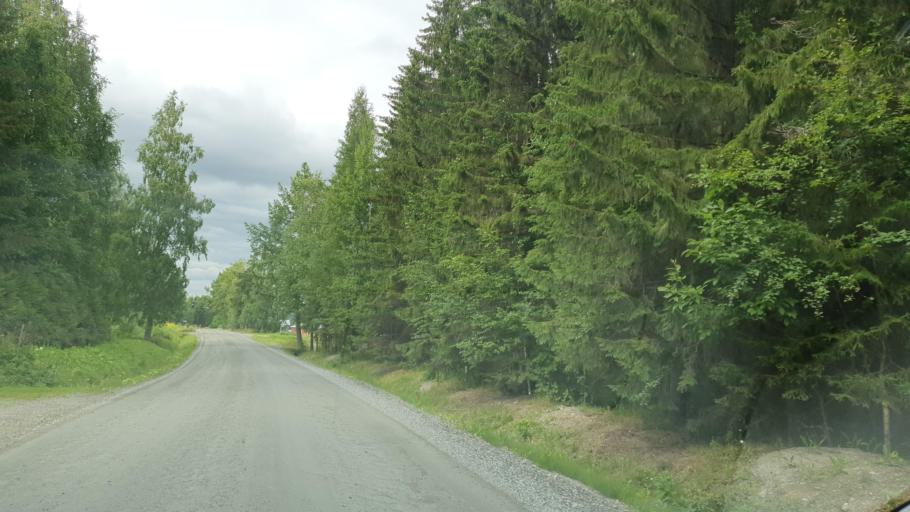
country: FI
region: Northern Savo
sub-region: Ylae-Savo
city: Iisalmi
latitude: 63.5331
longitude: 27.0880
